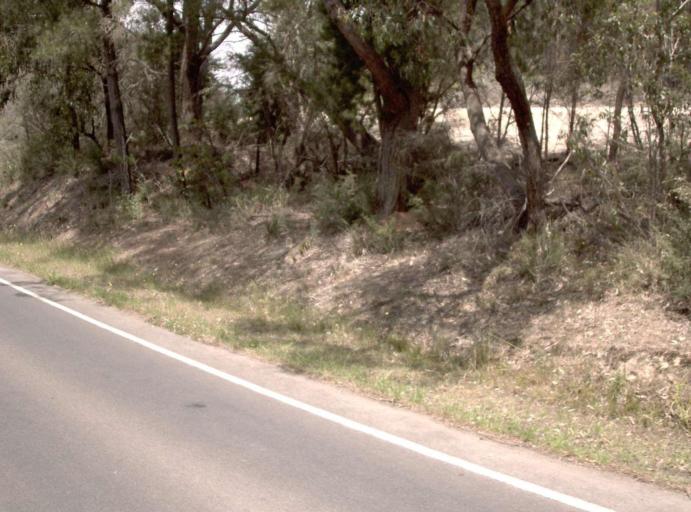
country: AU
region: Victoria
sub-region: Latrobe
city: Traralgon
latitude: -38.2767
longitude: 146.6937
